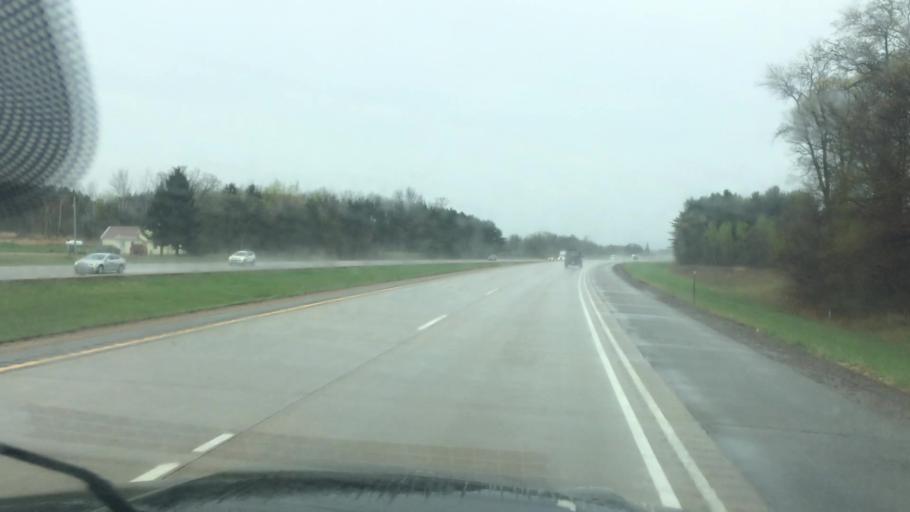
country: US
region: Wisconsin
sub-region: Portage County
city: Stevens Point
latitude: 44.6445
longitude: -89.6363
